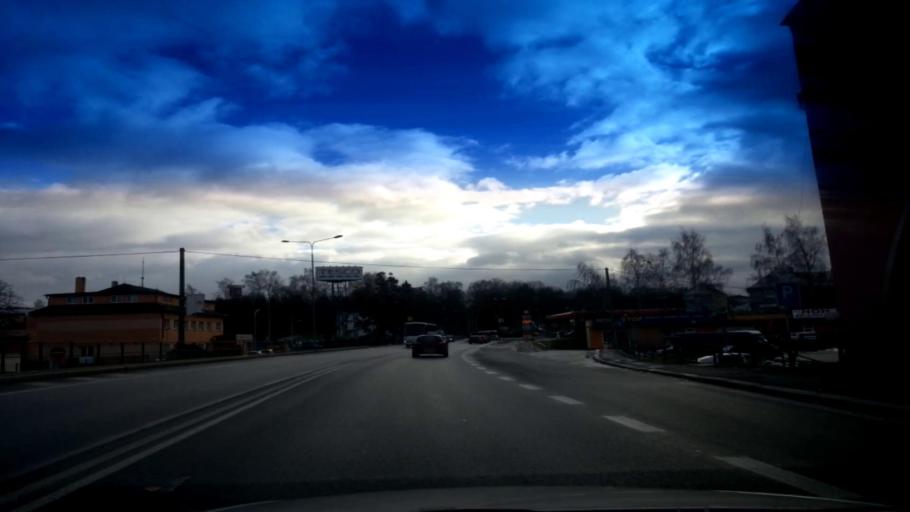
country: CZ
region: Karlovarsky
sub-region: Okres Cheb
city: Cheb
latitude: 50.0820
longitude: 12.3752
